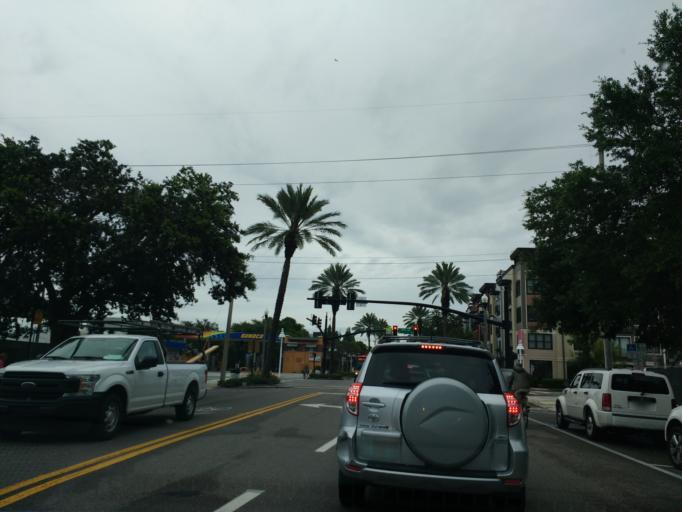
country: US
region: Florida
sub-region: Pinellas County
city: Saint Petersburg
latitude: 27.7711
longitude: -82.6554
